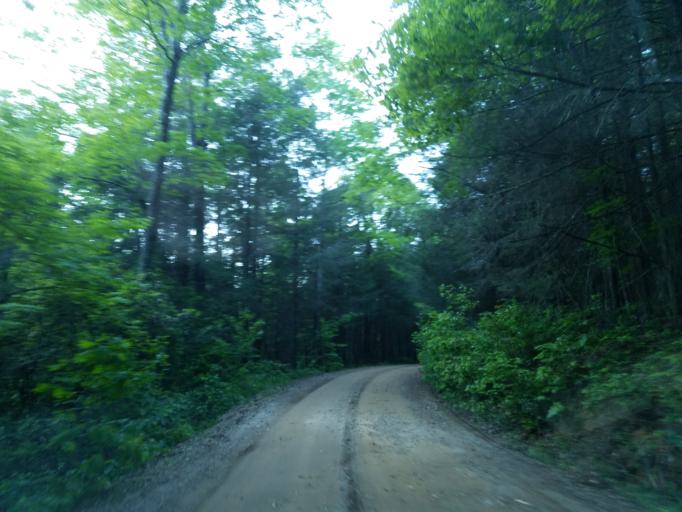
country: US
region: Georgia
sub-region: Lumpkin County
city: Dahlonega
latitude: 34.6862
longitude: -84.1407
